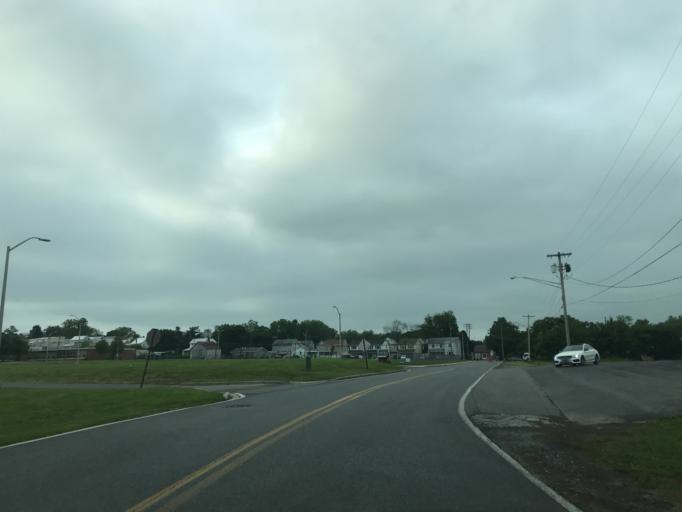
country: US
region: Maryland
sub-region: Frederick County
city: Emmitsburg
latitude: 39.7011
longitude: -77.3212
